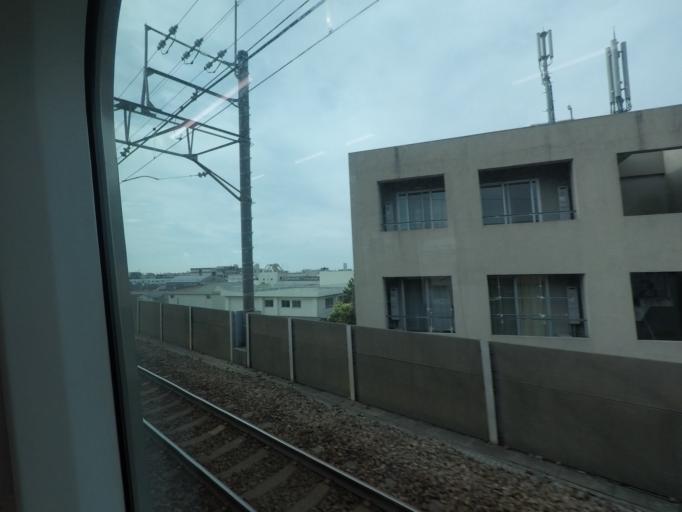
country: JP
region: Kanagawa
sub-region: Kawasaki-shi
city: Kawasaki
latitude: 35.5776
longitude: 139.6476
